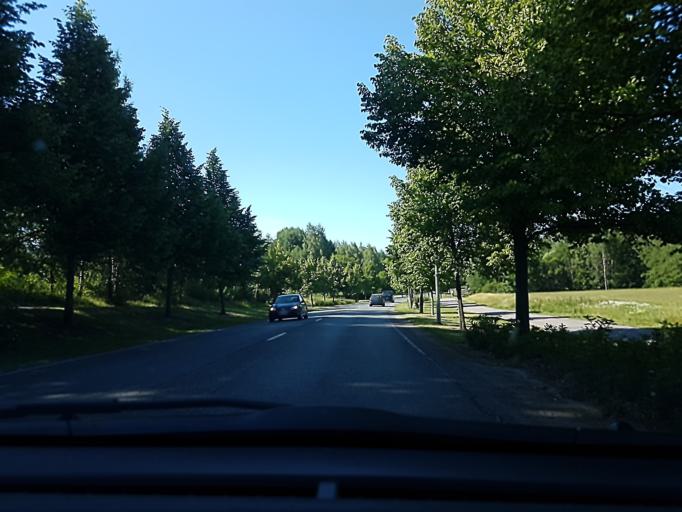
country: FI
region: Uusimaa
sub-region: Helsinki
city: Vantaa
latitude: 60.3435
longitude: 25.0737
